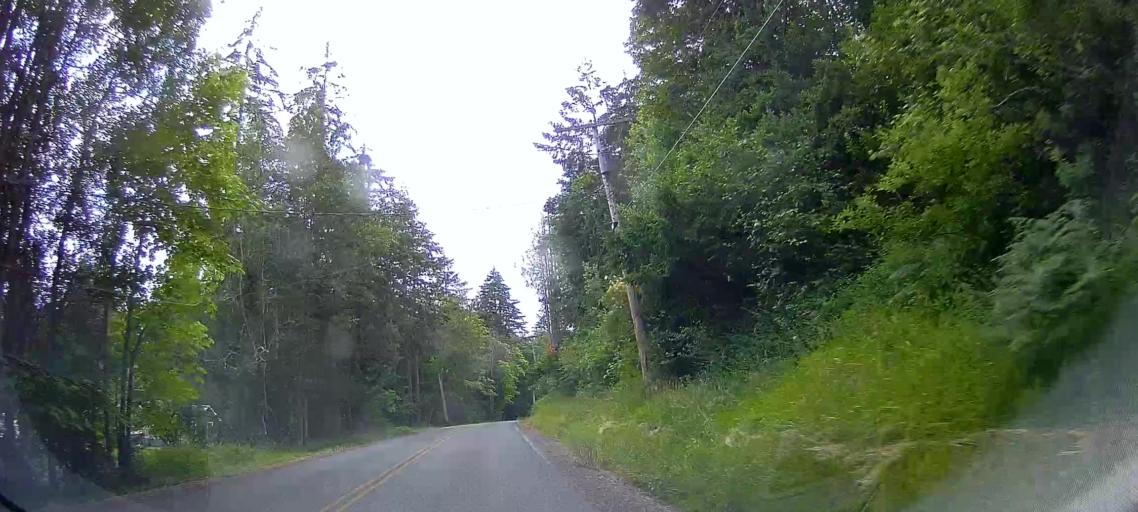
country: US
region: Washington
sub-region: Skagit County
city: Mount Vernon
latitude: 48.3656
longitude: -122.4235
